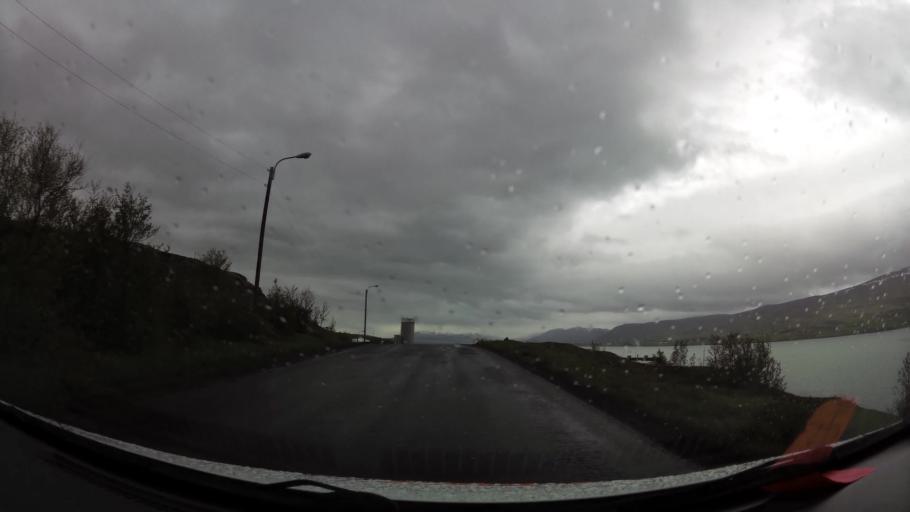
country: IS
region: Northeast
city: Akureyri
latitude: 65.6998
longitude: -18.1167
